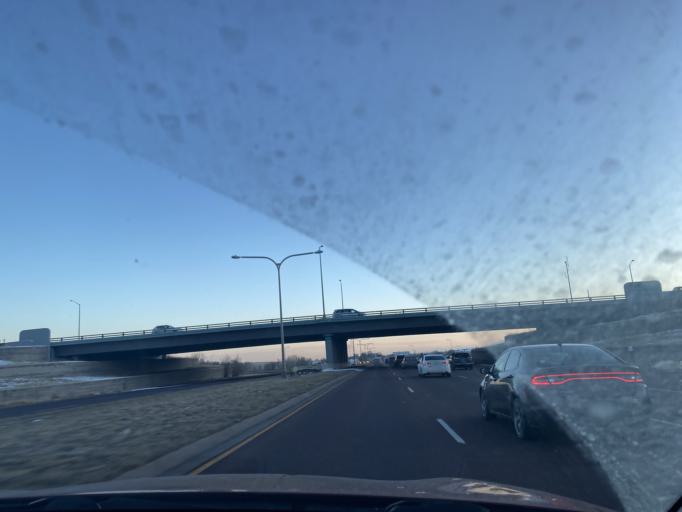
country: US
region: Colorado
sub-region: El Paso County
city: Cimarron Hills
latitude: 38.8401
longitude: -104.7209
